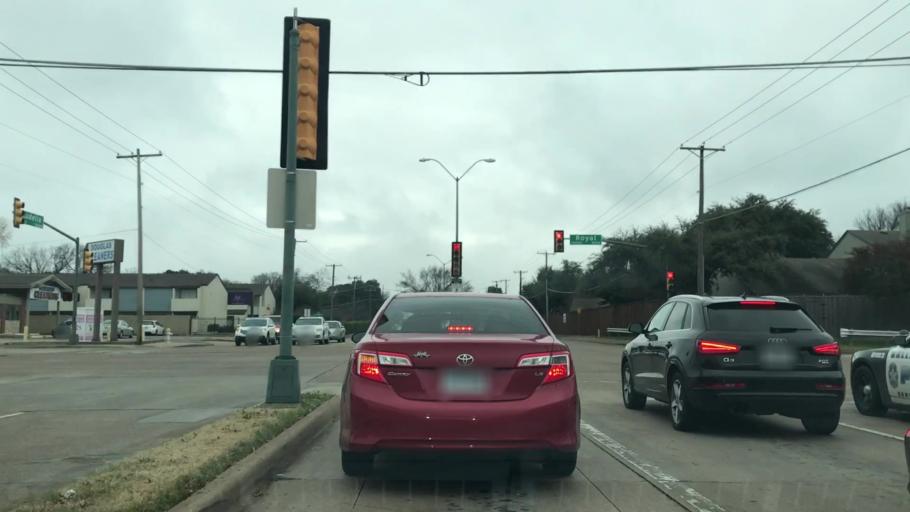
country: US
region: Texas
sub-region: Dallas County
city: Richardson
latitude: 32.8948
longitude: -96.7179
